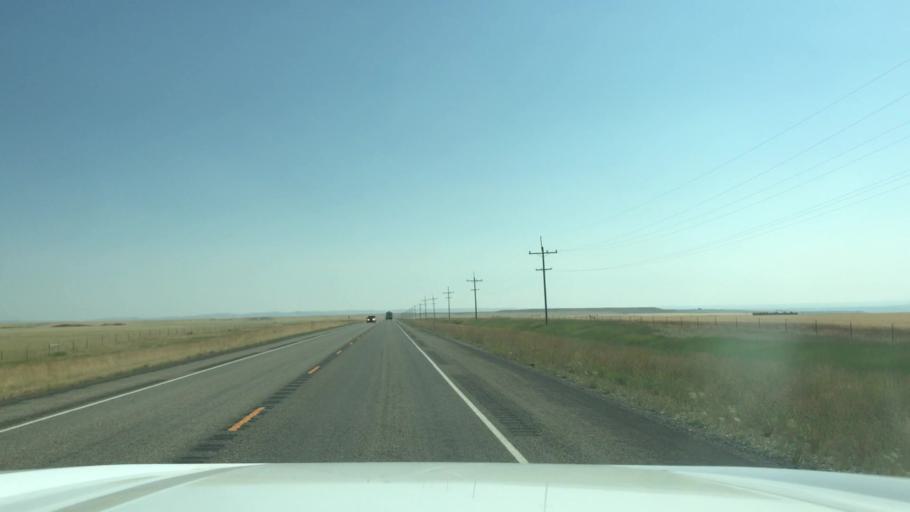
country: US
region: Montana
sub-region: Wheatland County
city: Harlowton
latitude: 46.5067
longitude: -109.7660
